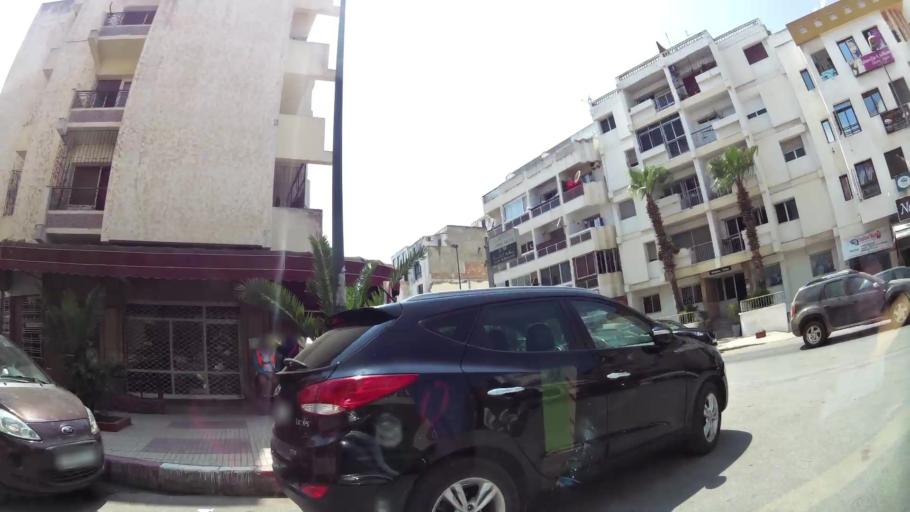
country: MA
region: Rabat-Sale-Zemmour-Zaer
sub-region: Rabat
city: Rabat
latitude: 34.0046
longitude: -6.8491
